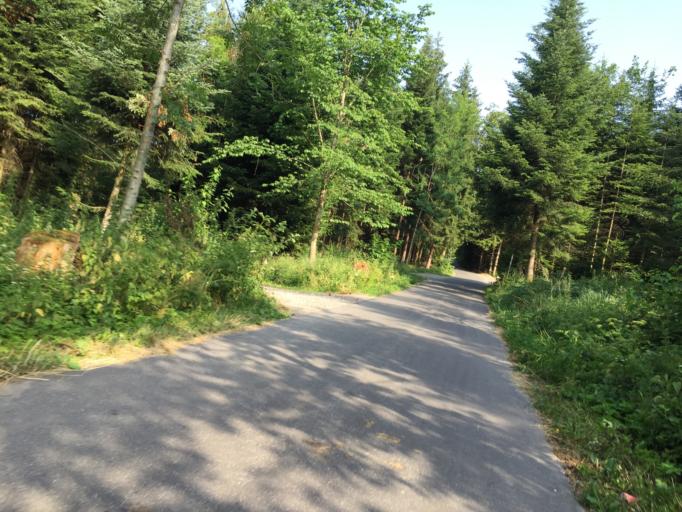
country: CH
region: Bern
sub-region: Bern-Mittelland District
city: Muri
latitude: 46.9261
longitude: 7.5171
